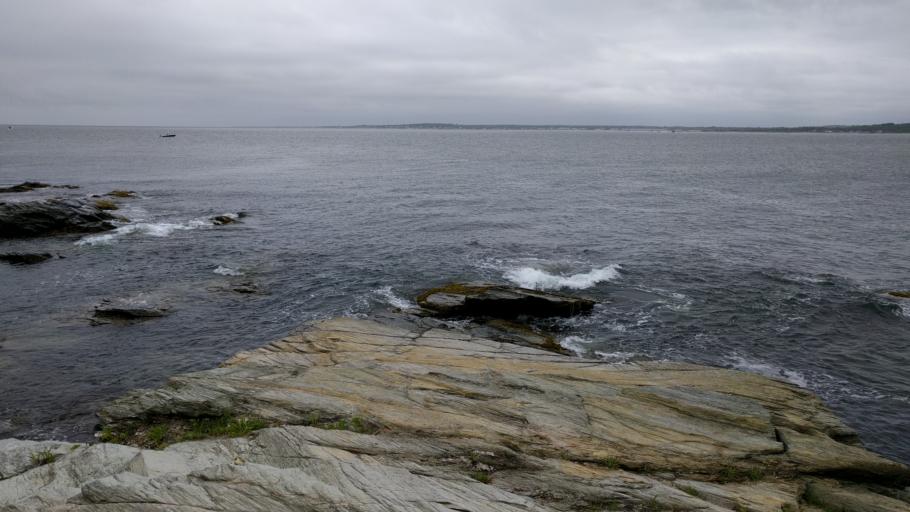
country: US
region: Rhode Island
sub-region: Newport County
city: Jamestown
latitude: 41.4512
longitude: -71.4001
